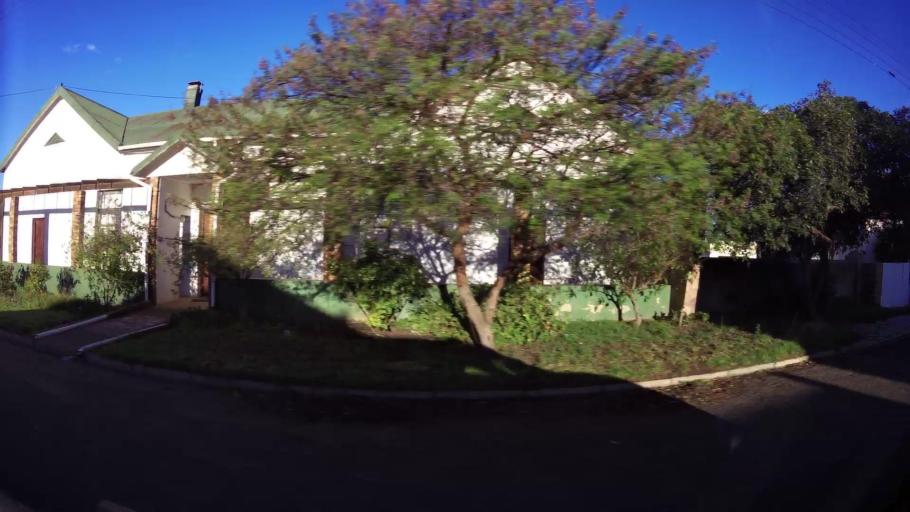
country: ZA
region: Western Cape
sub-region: Eden District Municipality
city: Riversdale
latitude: -34.0886
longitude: 20.9600
